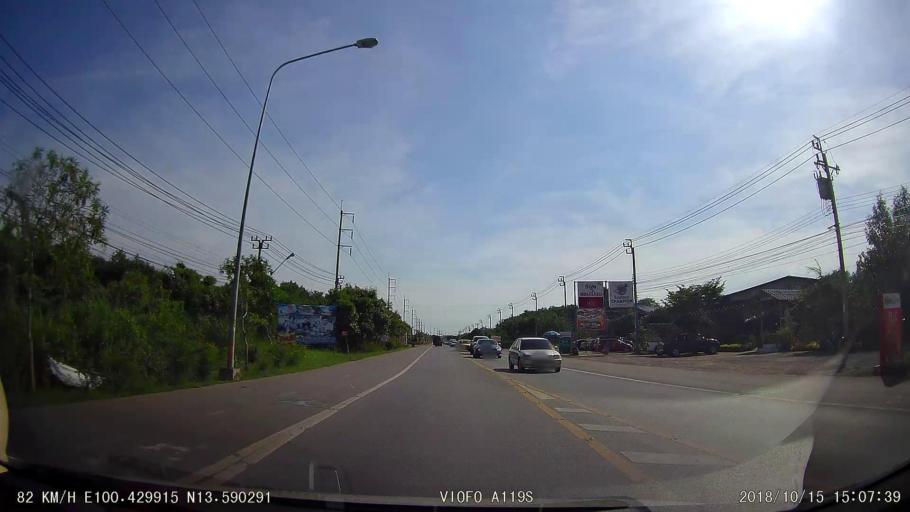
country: TH
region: Bangkok
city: Bang Khun Thian
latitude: 13.5903
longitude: 100.4299
